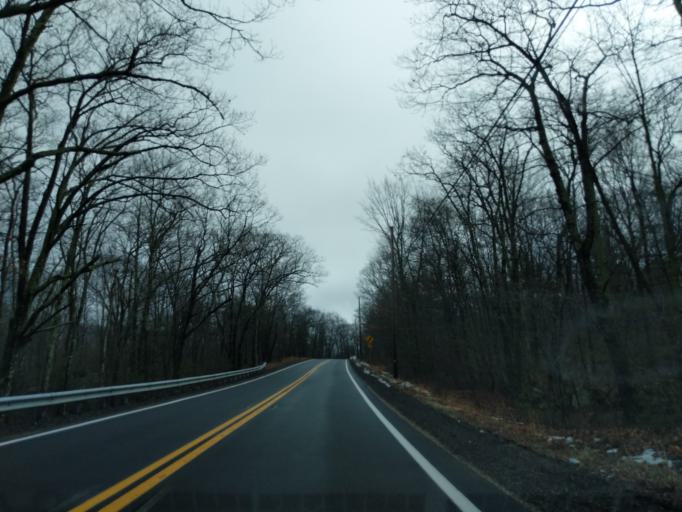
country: US
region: Massachusetts
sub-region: Worcester County
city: Douglas
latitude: 42.0576
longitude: -71.8008
